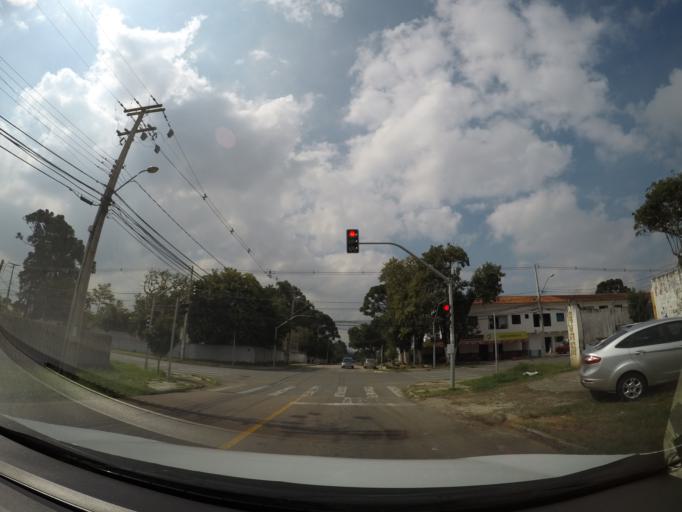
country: BR
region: Parana
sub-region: Sao Jose Dos Pinhais
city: Sao Jose dos Pinhais
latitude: -25.4999
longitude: -49.2454
